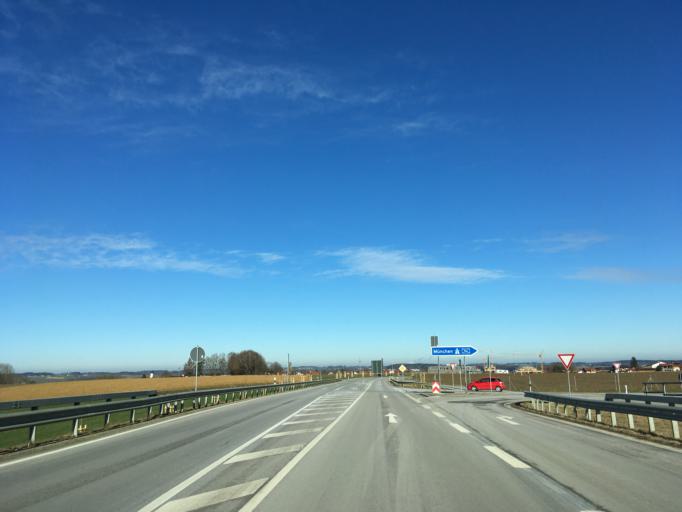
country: DE
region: Bavaria
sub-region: Upper Bavaria
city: Obertaufkirchen
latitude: 48.2503
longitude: 12.2820
